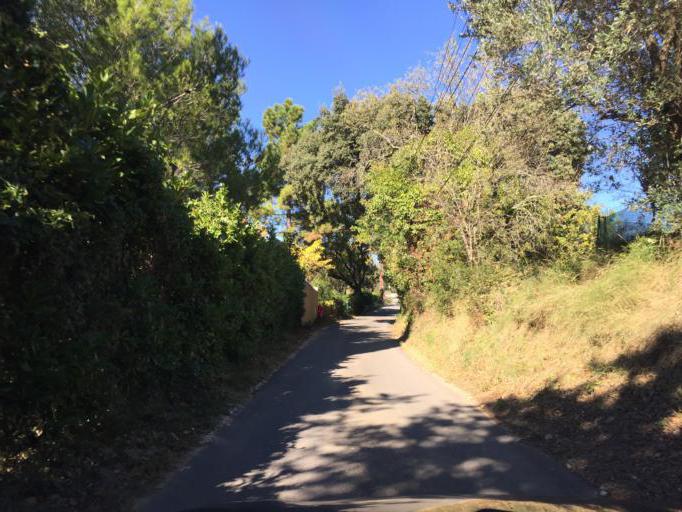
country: FR
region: Provence-Alpes-Cote d'Azur
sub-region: Departement du Vaucluse
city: Piolenc
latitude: 44.1946
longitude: 4.7529
